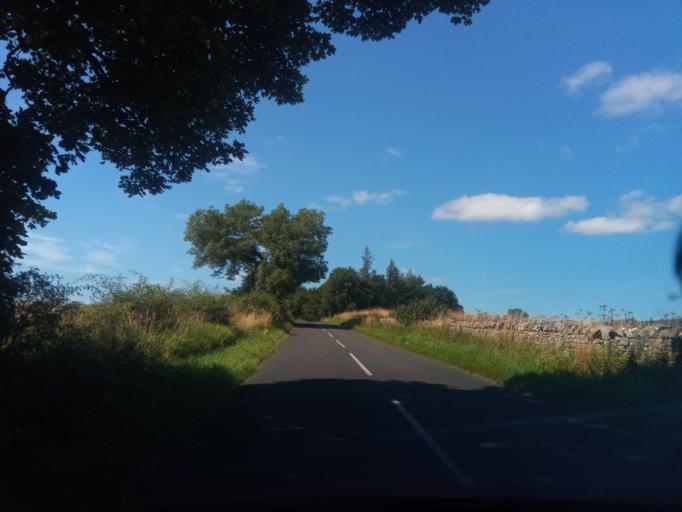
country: GB
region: England
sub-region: Northumberland
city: Wall
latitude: 55.0132
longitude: -2.1541
